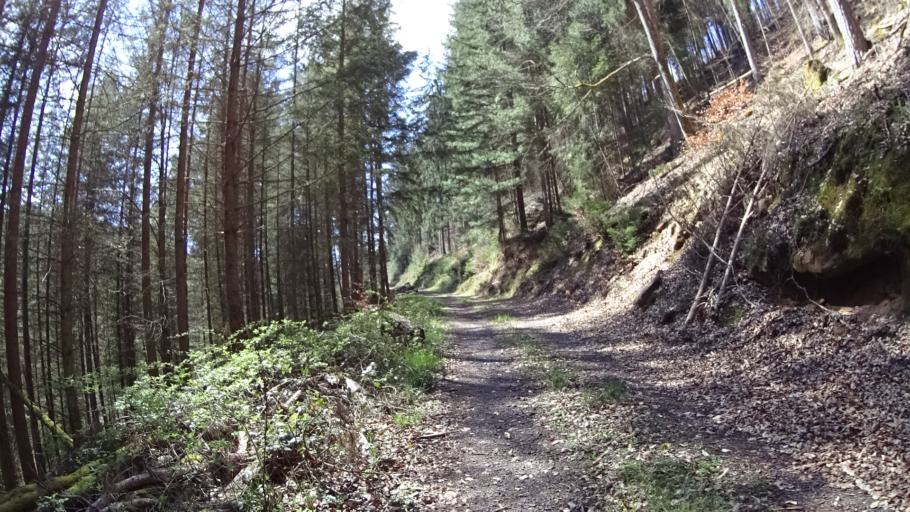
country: DE
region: Rheinland-Pfalz
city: Esthal
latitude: 49.3262
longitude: 7.9954
